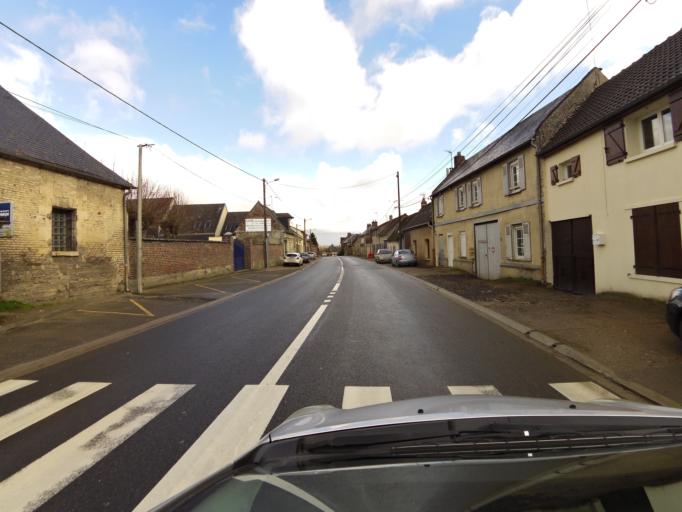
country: FR
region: Picardie
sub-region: Departement de l'Oise
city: Ressons-sur-Matz
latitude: 49.5767
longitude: 2.7073
